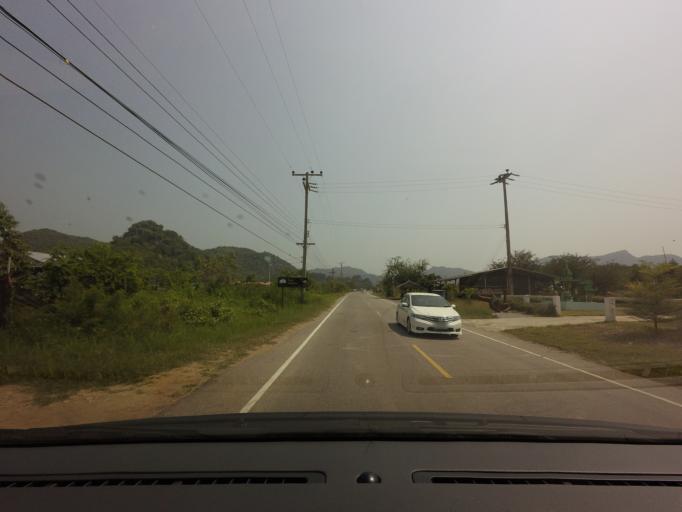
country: TH
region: Prachuap Khiri Khan
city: Sam Roi Yot
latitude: 12.1949
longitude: 99.9900
